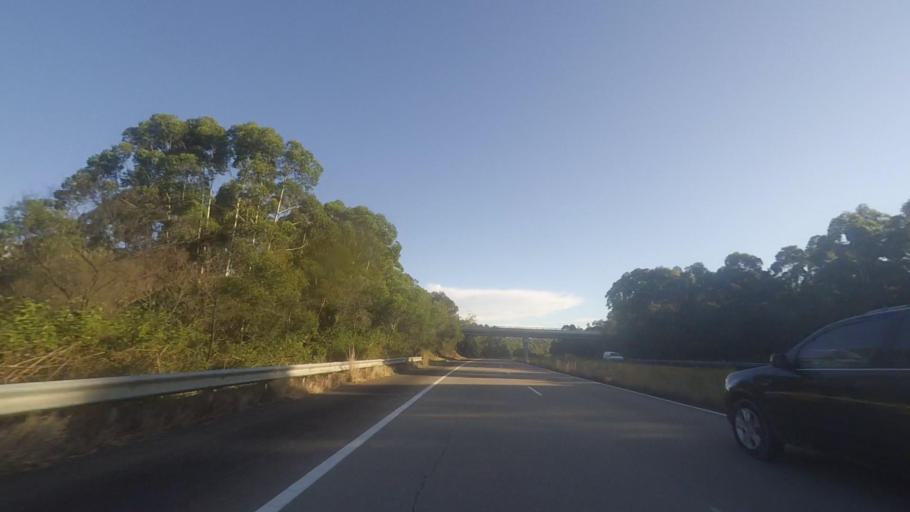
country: AU
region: New South Wales
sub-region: Great Lakes
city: Bulahdelah
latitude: -32.3004
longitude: 152.3462
